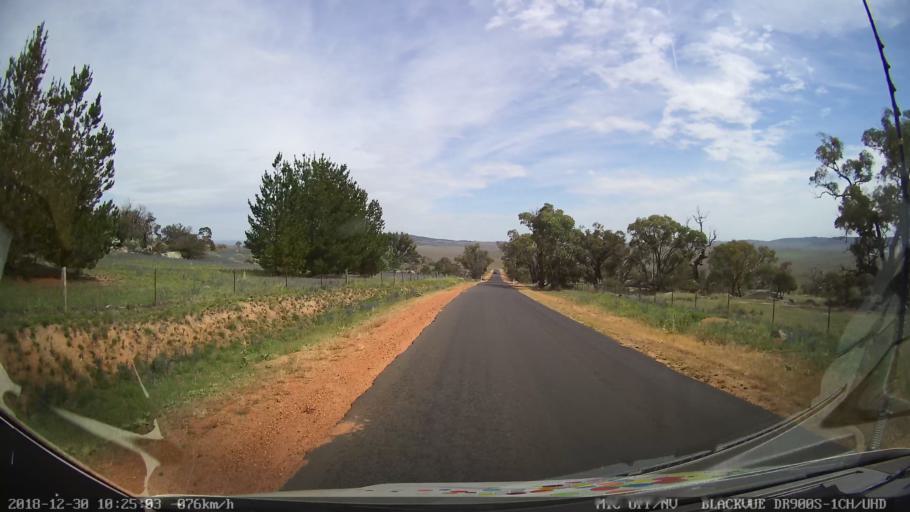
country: AU
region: New South Wales
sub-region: Snowy River
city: Berridale
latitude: -36.5291
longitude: 148.9620
